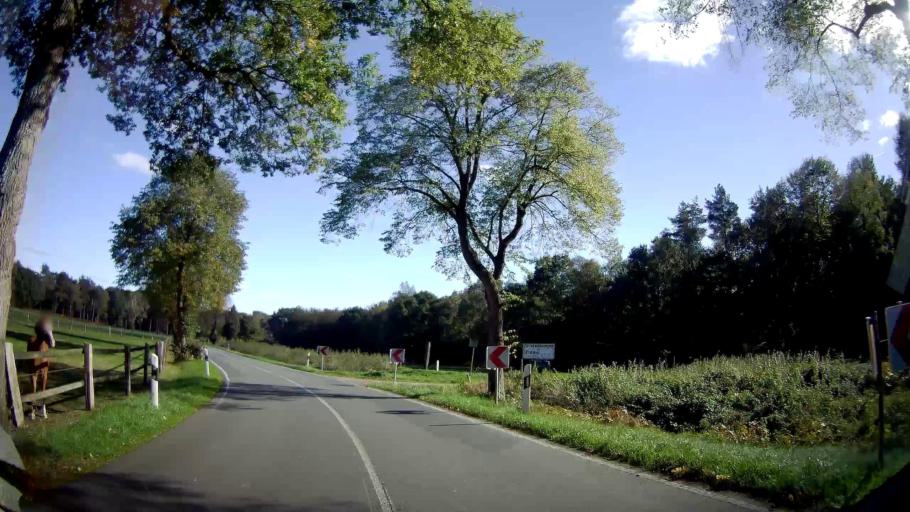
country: DE
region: North Rhine-Westphalia
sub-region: Regierungsbezirk Dusseldorf
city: Hunxe
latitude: 51.6137
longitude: 6.8106
